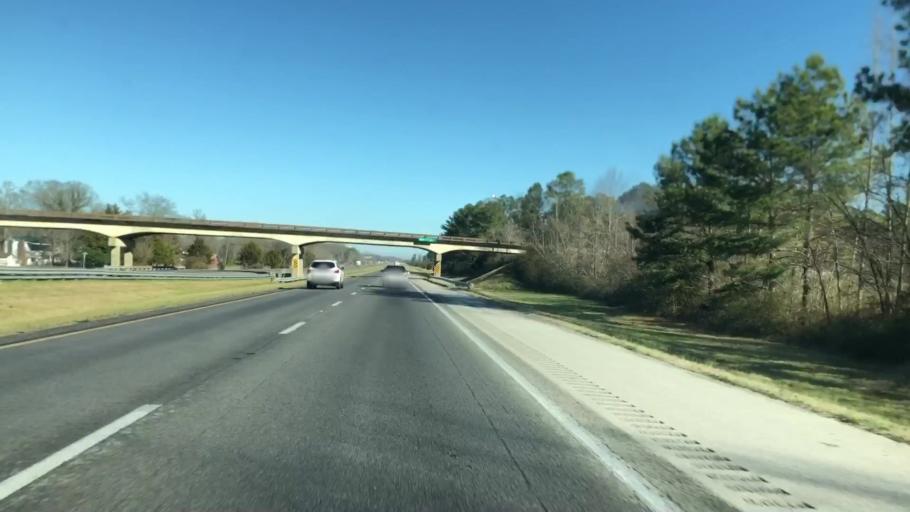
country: US
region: Alabama
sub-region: Limestone County
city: Athens
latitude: 34.8605
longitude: -86.9263
